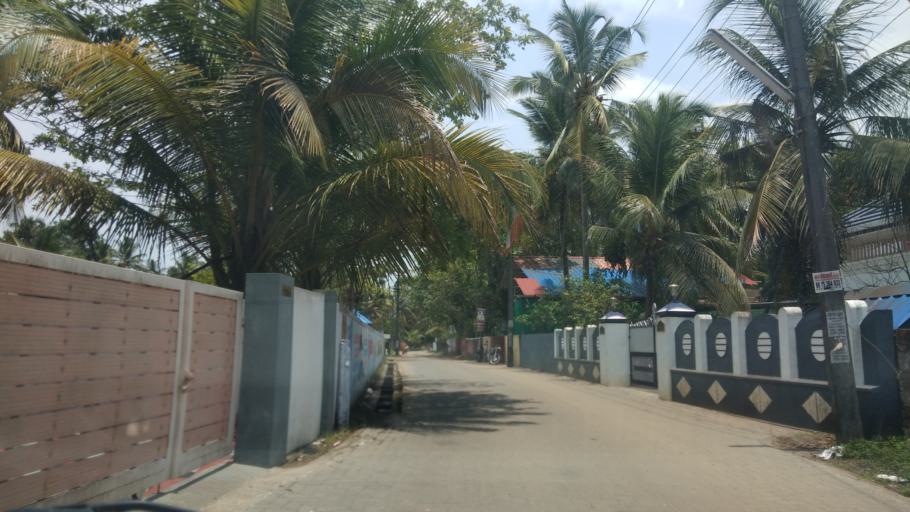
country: IN
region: Kerala
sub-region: Alappuzha
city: Arukutti
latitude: 9.8984
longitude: 76.3103
